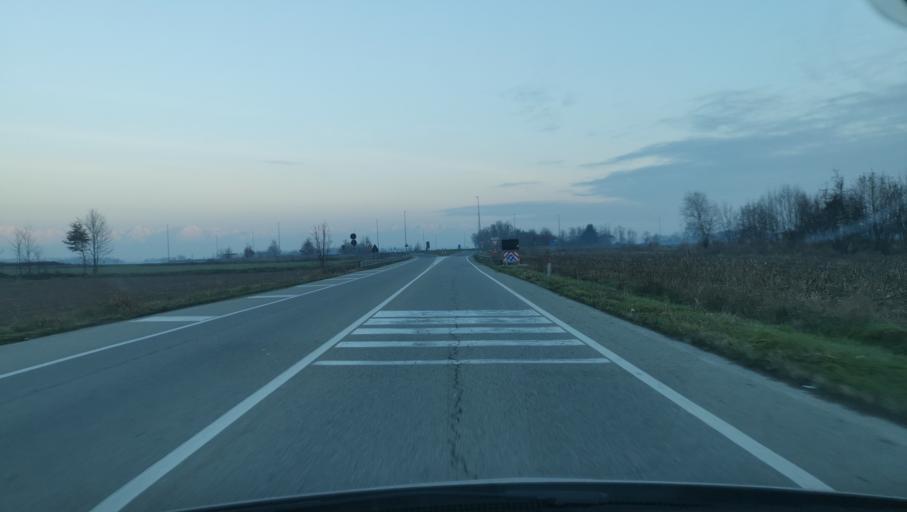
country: IT
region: Piedmont
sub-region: Provincia di Torino
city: Chivasso
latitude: 45.2267
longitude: 7.8908
